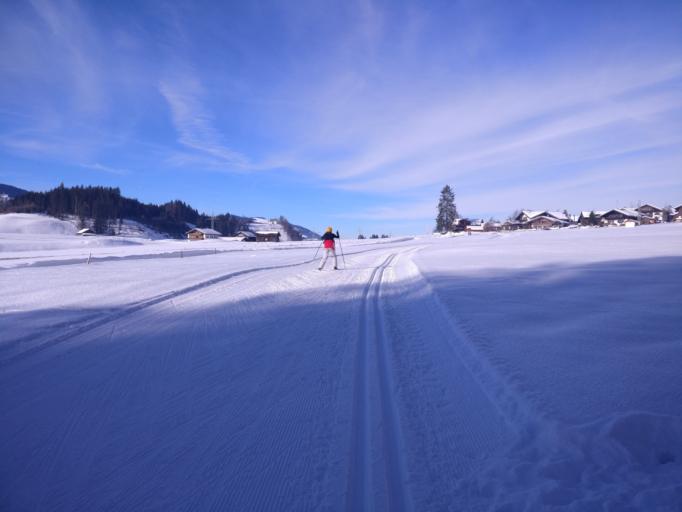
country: DE
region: Bavaria
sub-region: Swabia
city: Oberstdorf
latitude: 47.4399
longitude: 10.2929
